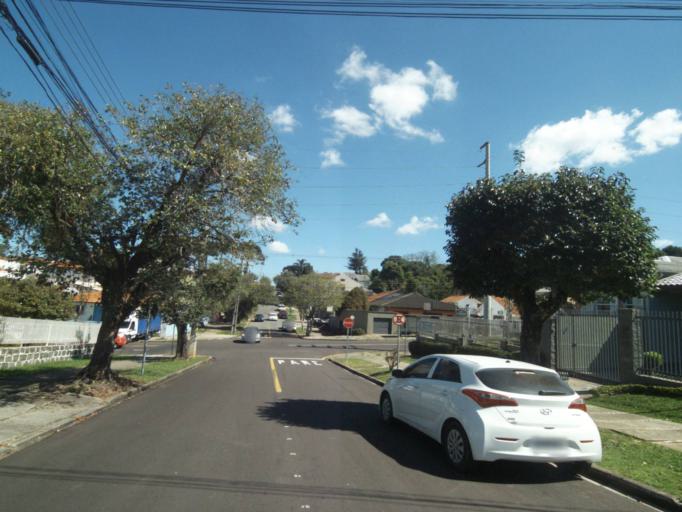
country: BR
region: Parana
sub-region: Curitiba
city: Curitiba
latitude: -25.4044
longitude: -49.2725
